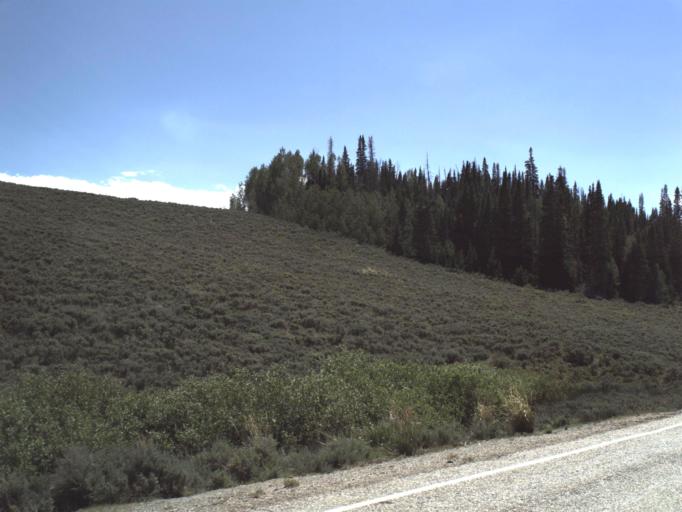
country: US
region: Utah
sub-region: Rich County
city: Randolph
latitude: 41.4847
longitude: -111.4072
